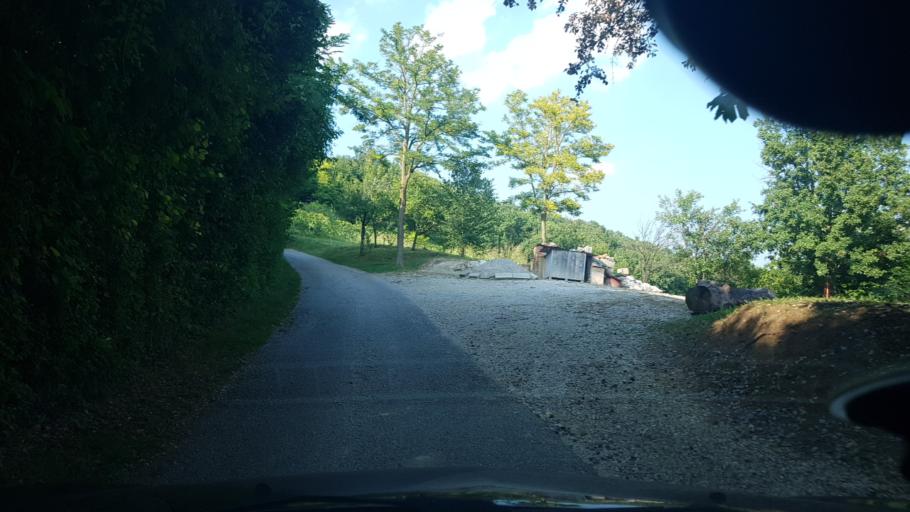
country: HR
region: Krapinsko-Zagorska
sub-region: Grad Krapina
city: Krapina
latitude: 46.1676
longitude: 15.8956
